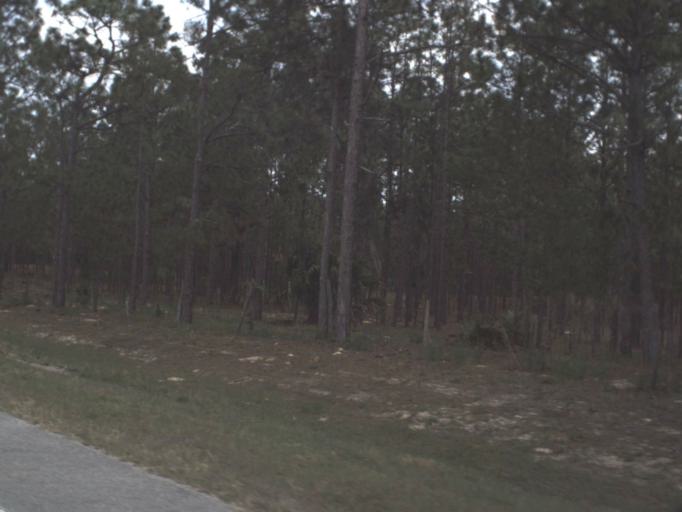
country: US
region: Florida
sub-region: Lake County
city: Mount Plymouth
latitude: 28.8524
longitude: -81.5267
